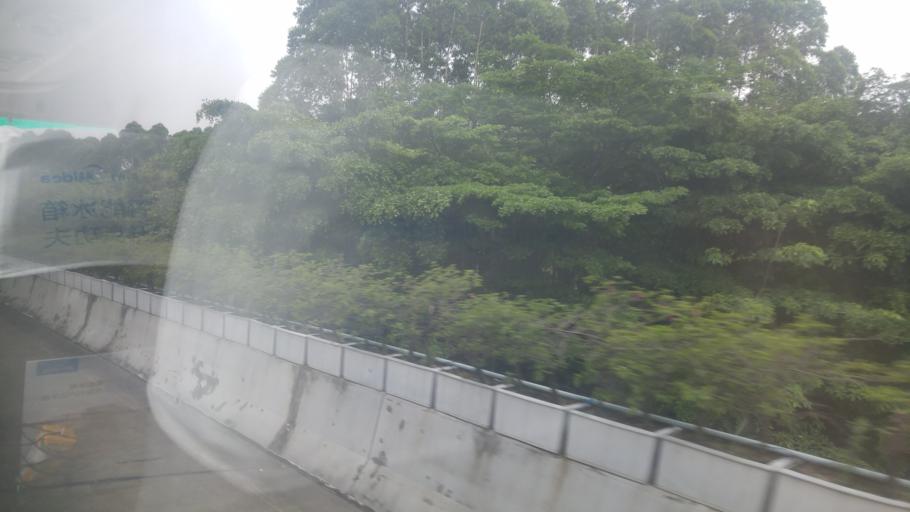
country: CN
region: Guangdong
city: Dali
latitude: 23.1364
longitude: 113.1279
